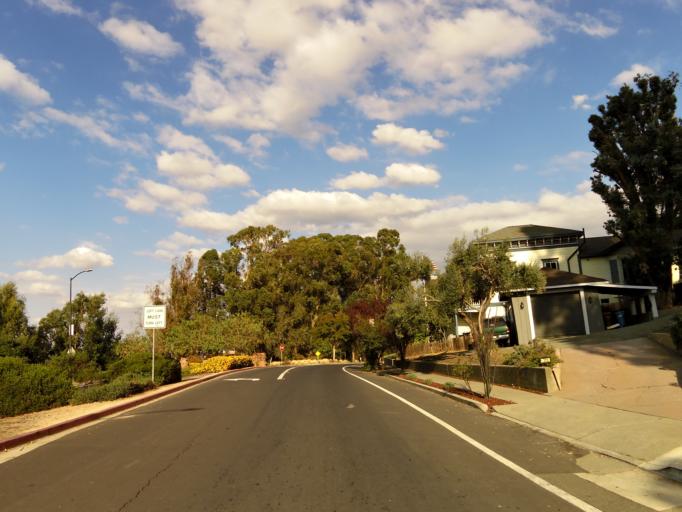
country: US
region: California
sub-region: Contra Costa County
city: Martinez
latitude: 38.0212
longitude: -122.1312
